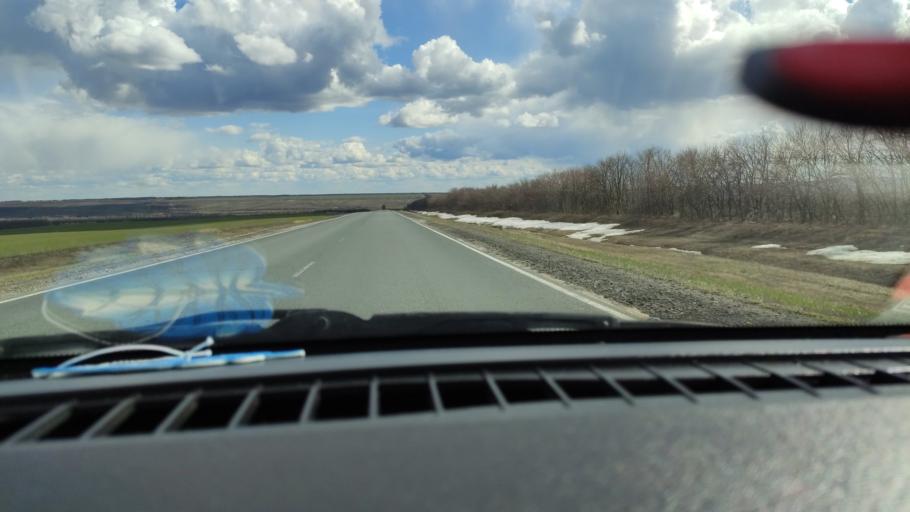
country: RU
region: Saratov
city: Dukhovnitskoye
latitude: 52.7611
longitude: 48.2412
